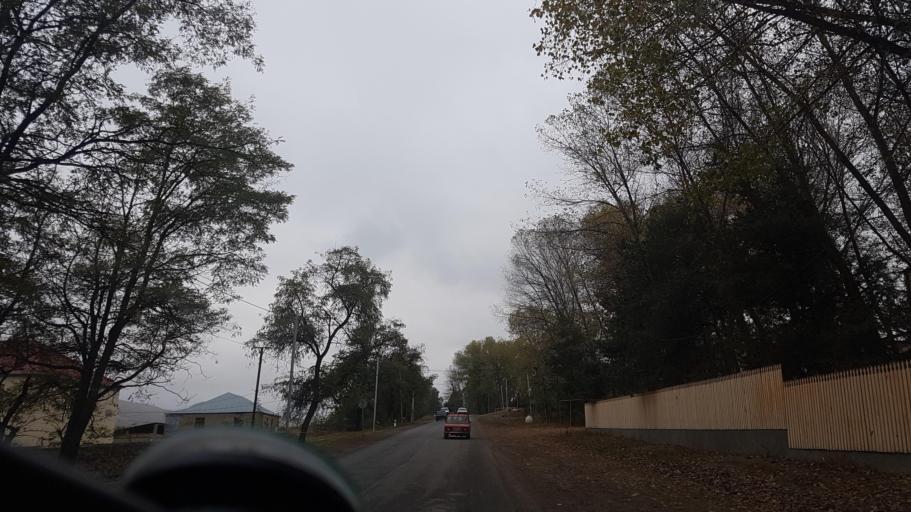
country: AZ
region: Gadabay Rayon
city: Ariqdam
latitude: 40.6509
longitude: 45.8088
